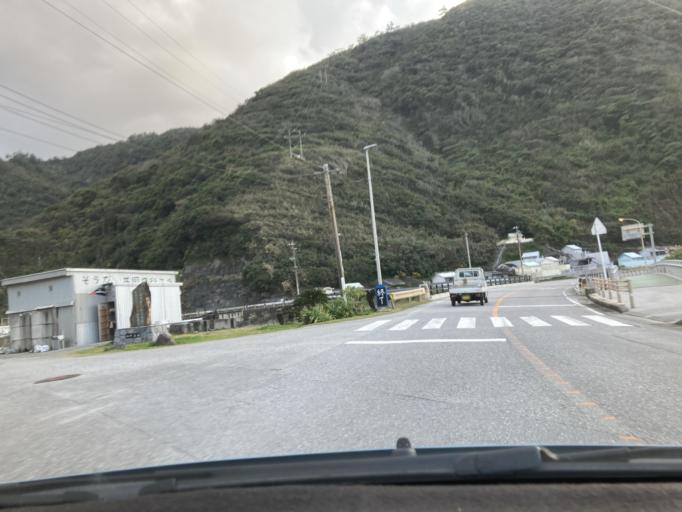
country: JP
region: Okinawa
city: Nago
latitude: 26.7980
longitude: 128.2325
